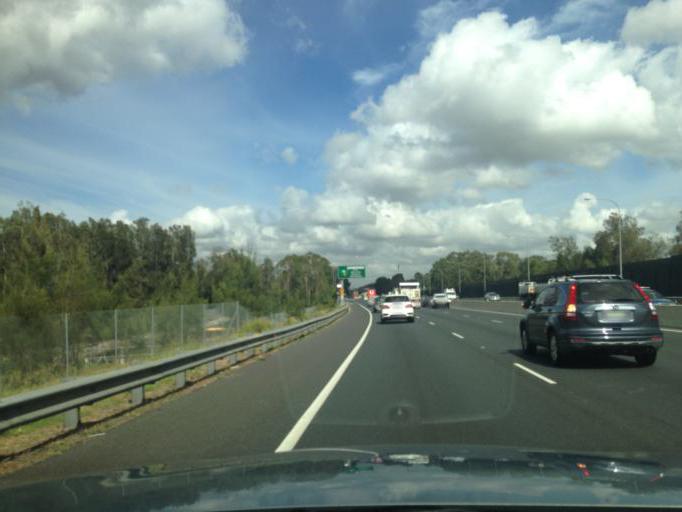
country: AU
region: New South Wales
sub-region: Bankstown
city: Milperra
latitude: -33.9436
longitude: 150.9899
